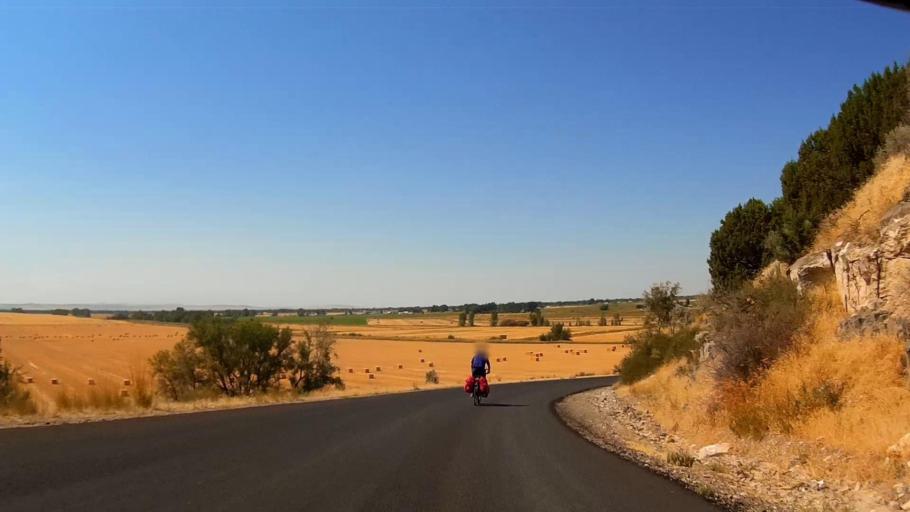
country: US
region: Idaho
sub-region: Madison County
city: Rexburg
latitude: 43.7156
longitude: -111.7522
